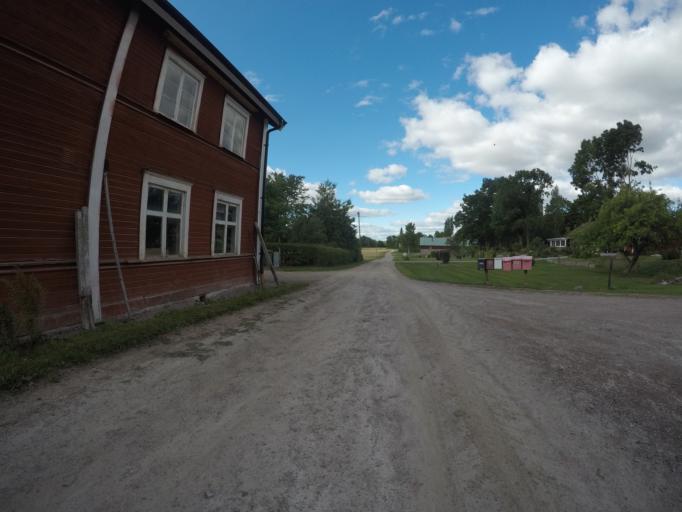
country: SE
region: Vaestmanland
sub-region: Hallstahammars Kommun
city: Kolback
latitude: 59.5211
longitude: 16.2161
